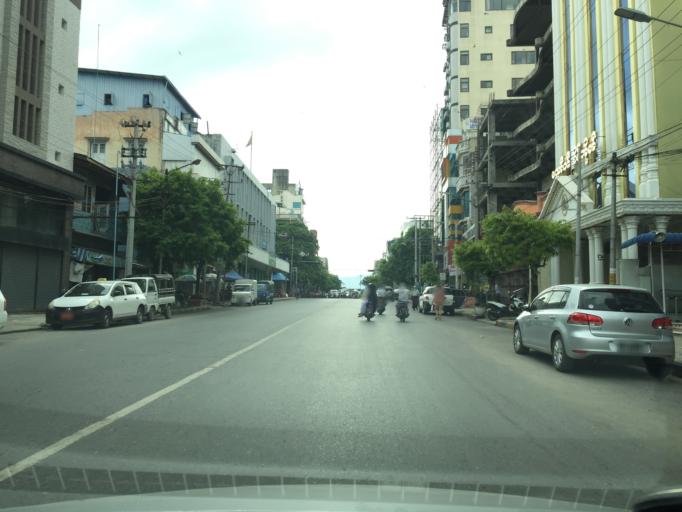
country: MM
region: Mandalay
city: Mandalay
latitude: 21.9834
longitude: 96.0802
